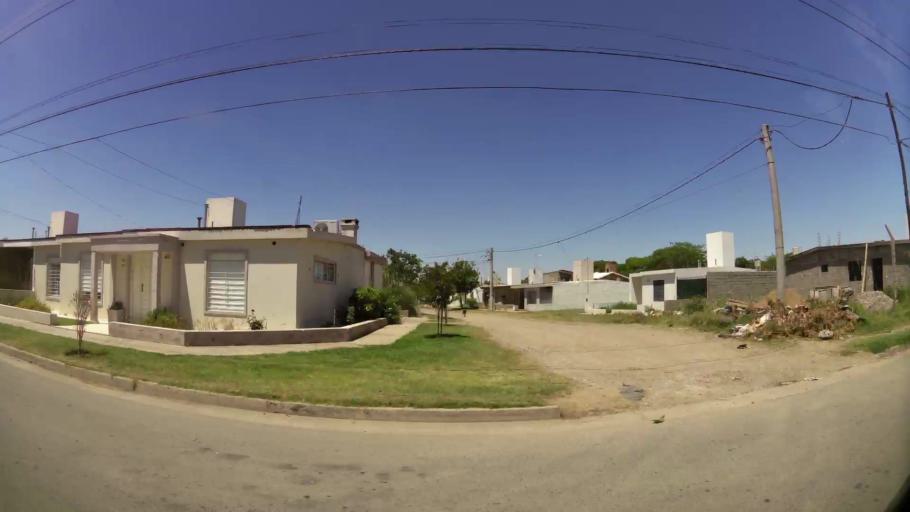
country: AR
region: Cordoba
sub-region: Departamento de Capital
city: Cordoba
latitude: -31.3874
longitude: -64.1428
